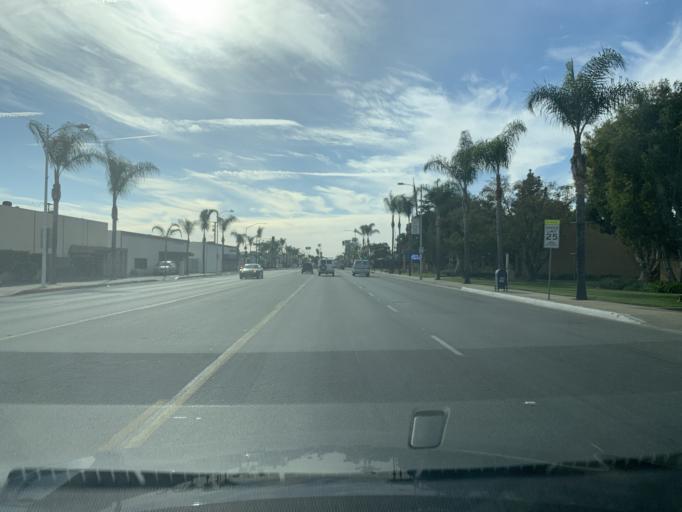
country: US
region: California
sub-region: Los Angeles County
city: South El Monte
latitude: 34.0448
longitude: -118.0454
